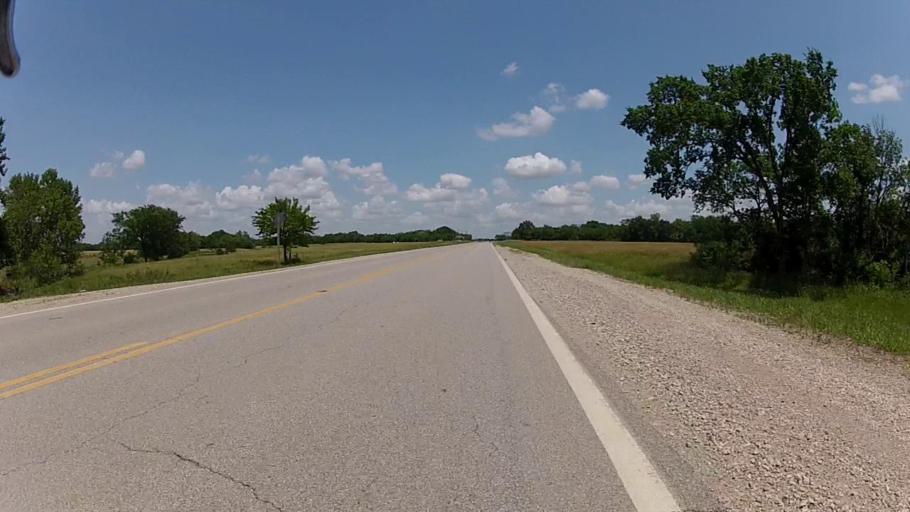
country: US
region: Kansas
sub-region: Labette County
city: Altamont
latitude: 37.1932
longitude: -95.4124
